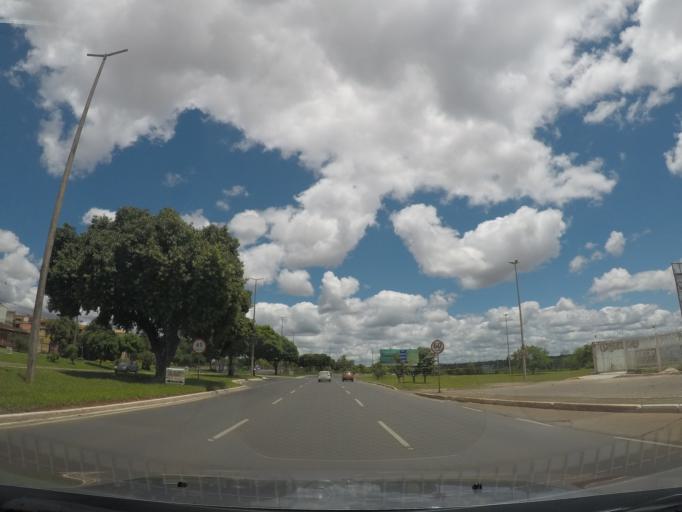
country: BR
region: Federal District
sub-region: Brasilia
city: Brasilia
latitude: -15.8392
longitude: -47.9664
